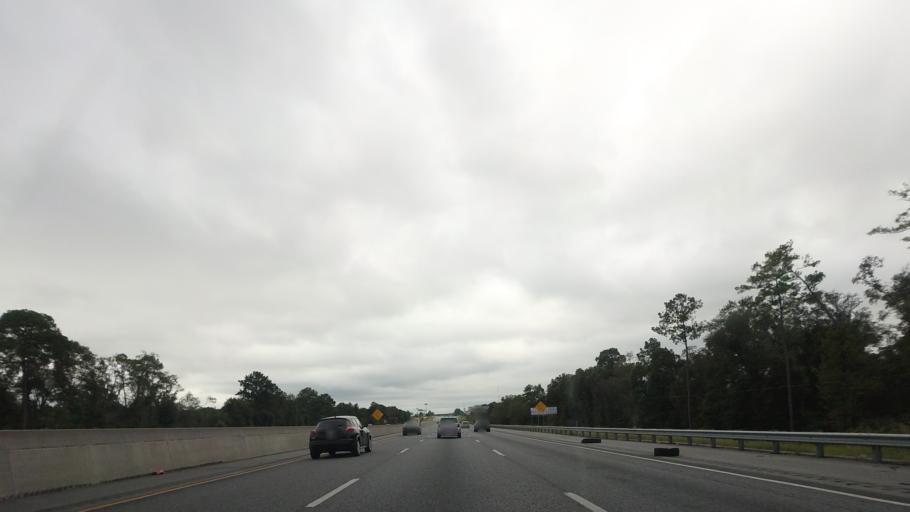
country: US
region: Georgia
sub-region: Lowndes County
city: Remerton
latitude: 30.8581
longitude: -83.3355
